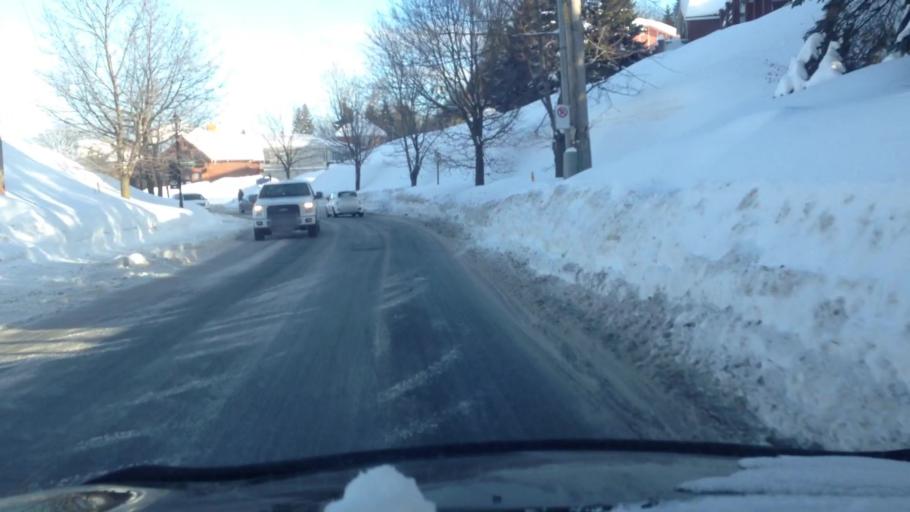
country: CA
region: Quebec
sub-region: Laurentides
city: Saint-Sauveur
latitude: 45.8901
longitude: -74.1512
